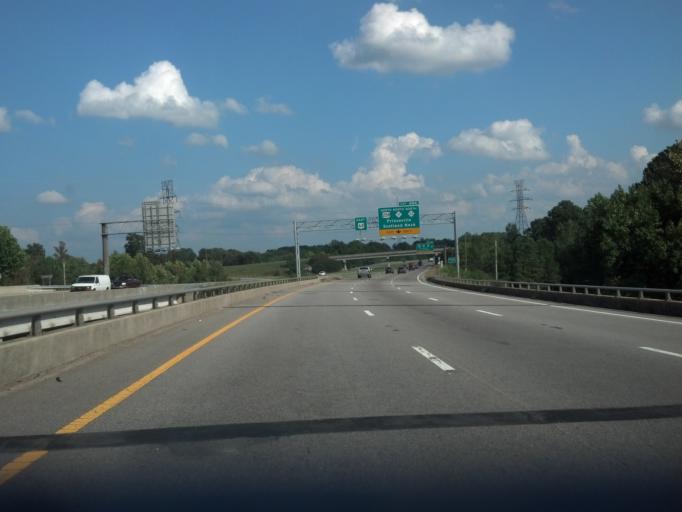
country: US
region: North Carolina
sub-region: Edgecombe County
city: Princeville
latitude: 35.8875
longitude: -77.5389
